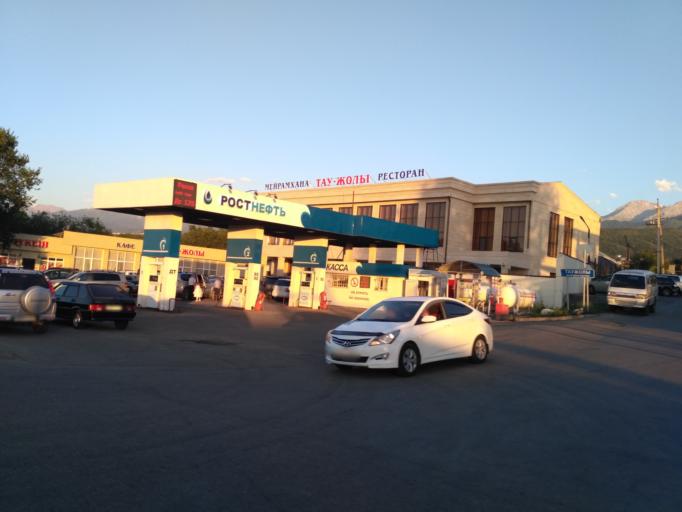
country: KZ
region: Almaty Qalasy
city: Almaty
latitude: 43.1750
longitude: 76.7899
